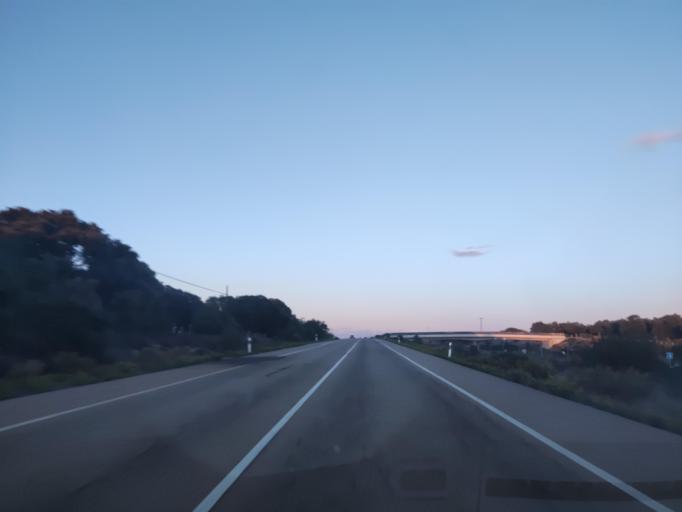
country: ES
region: Castille and Leon
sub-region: Provincia de Salamanca
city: San Munoz
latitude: 40.8162
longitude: -6.1292
